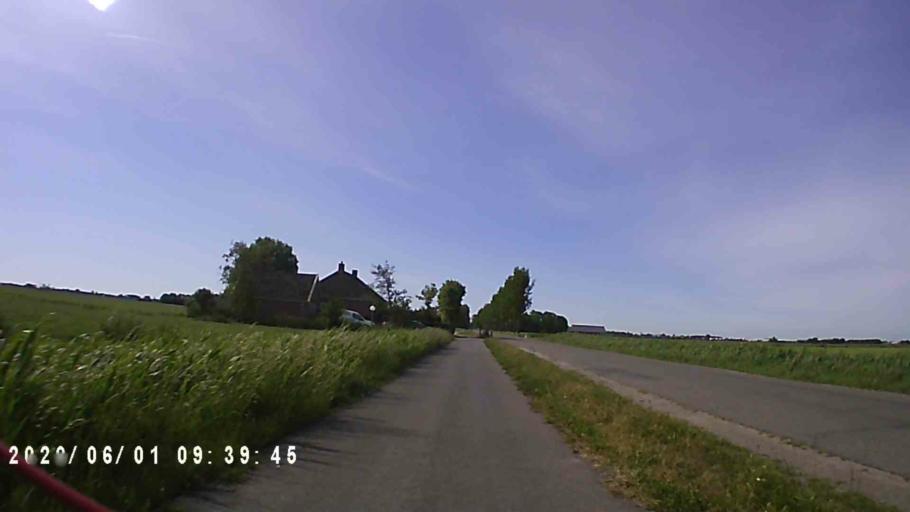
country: NL
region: Friesland
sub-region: Menameradiel
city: Berltsum
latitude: 53.2543
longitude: 5.6807
